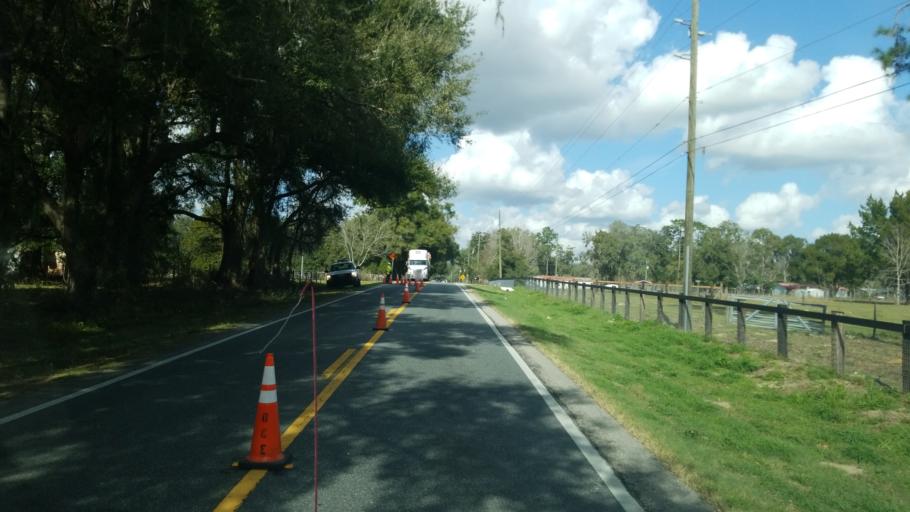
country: US
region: Florida
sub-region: Marion County
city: Belleview
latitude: 29.0017
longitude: -82.1199
